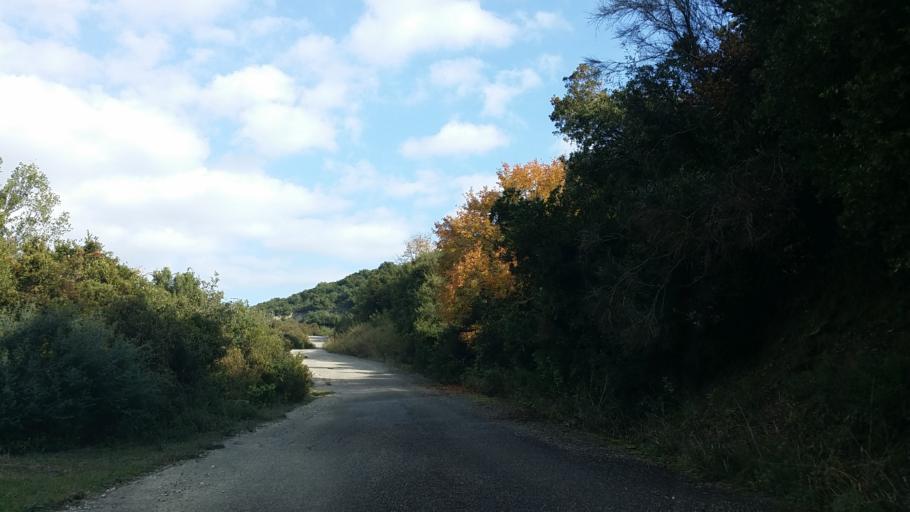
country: GR
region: West Greece
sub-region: Nomos Aitolias kai Akarnanias
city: Katouna
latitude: 38.8468
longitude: 21.0502
